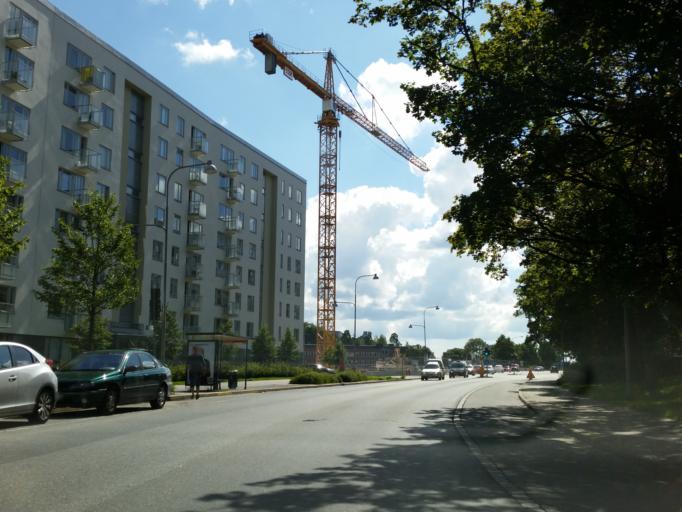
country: SE
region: Stockholm
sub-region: Solna Kommun
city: Solna
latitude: 59.3533
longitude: 18.0030
